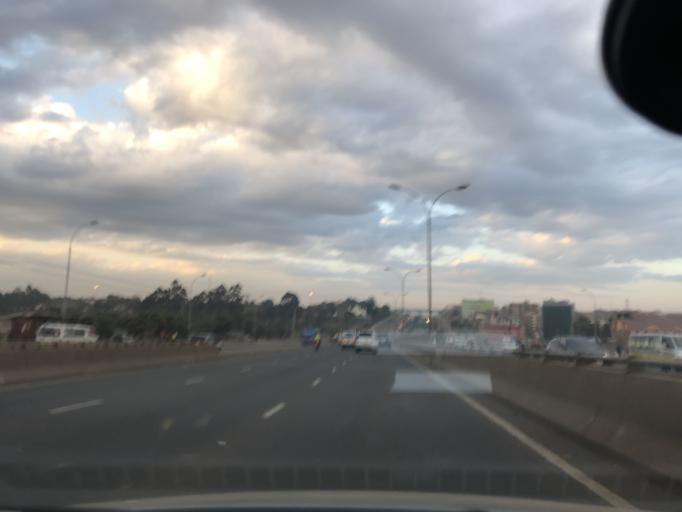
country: KE
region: Kiambu
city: Kiambu
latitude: -1.2021
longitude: 36.9184
